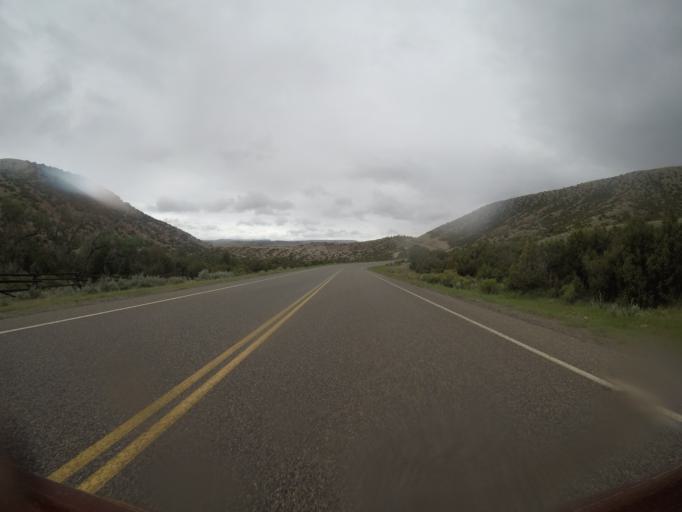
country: US
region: Wyoming
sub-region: Big Horn County
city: Lovell
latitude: 45.0808
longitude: -108.2599
